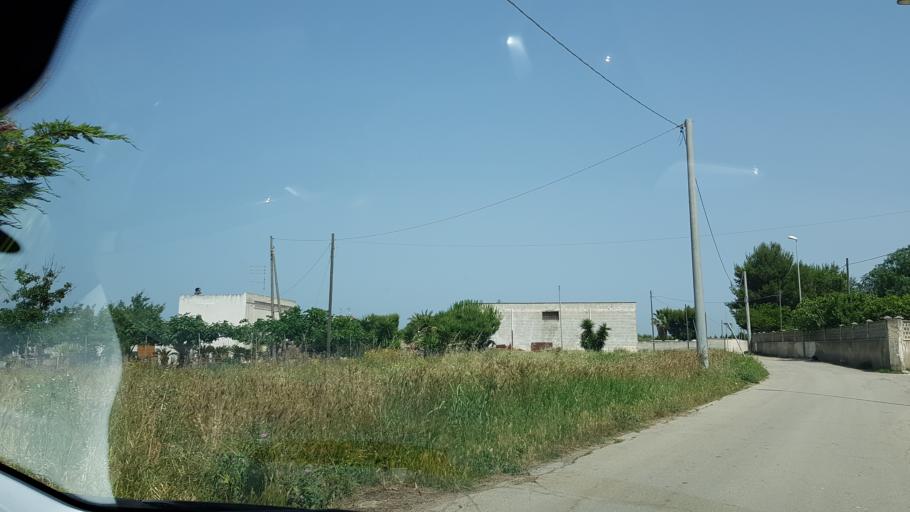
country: IT
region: Apulia
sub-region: Provincia di Brindisi
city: Mesagne
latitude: 40.5538
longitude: 17.8220
